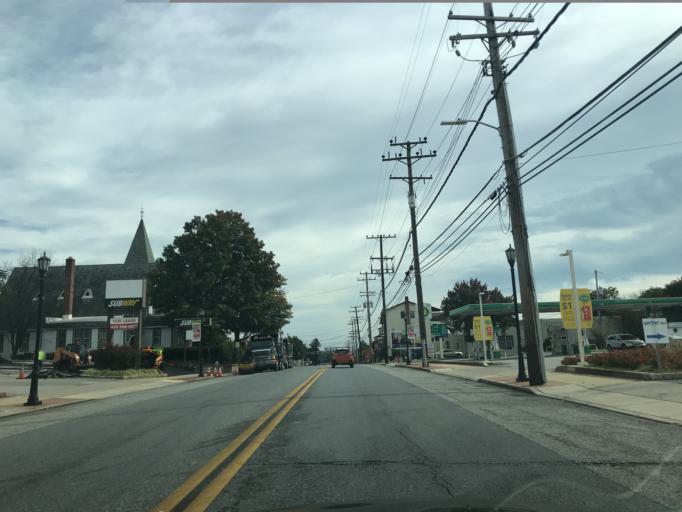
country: US
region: Maryland
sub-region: Baltimore County
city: Catonsville
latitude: 39.2724
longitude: -76.7298
